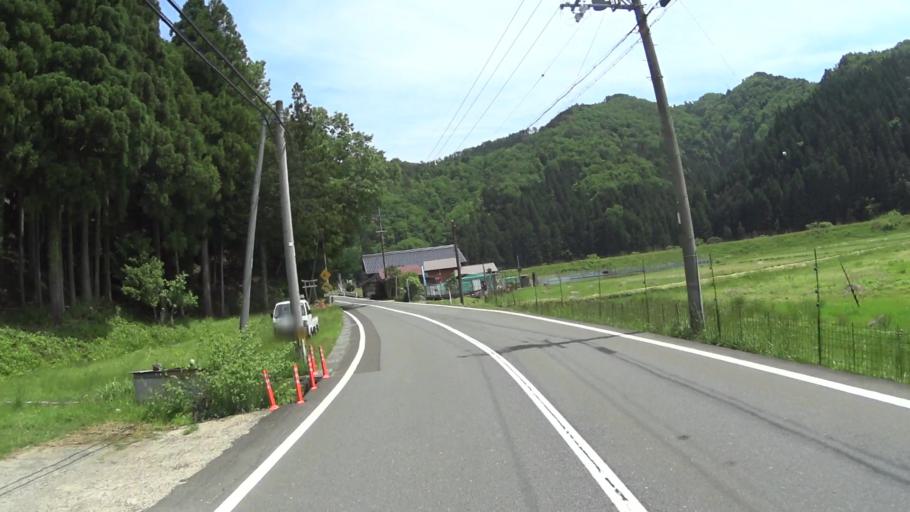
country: JP
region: Kyoto
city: Maizuru
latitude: 35.3859
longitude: 135.4591
